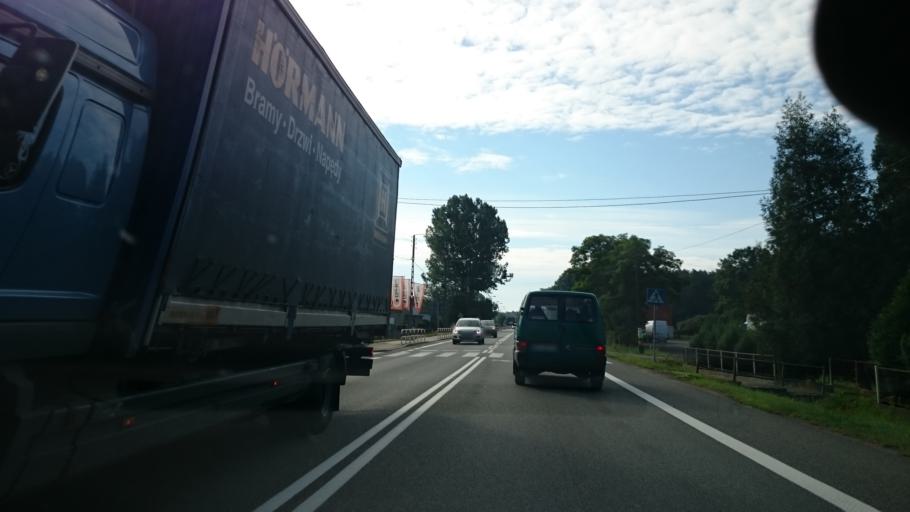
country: PL
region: Opole Voivodeship
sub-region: Powiat opolski
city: Tarnow Opolski
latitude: 50.6041
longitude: 18.0763
